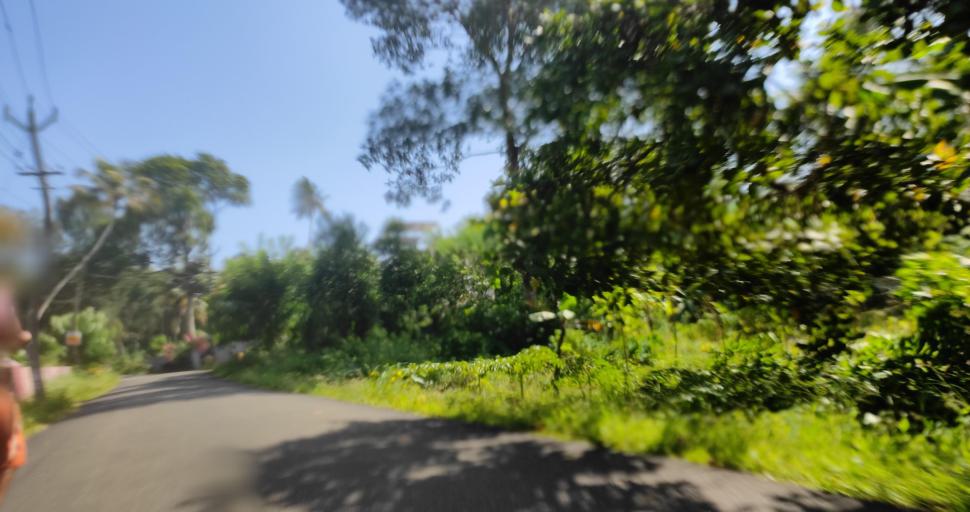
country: IN
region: Kerala
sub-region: Alappuzha
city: Shertallai
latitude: 9.6283
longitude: 76.3437
